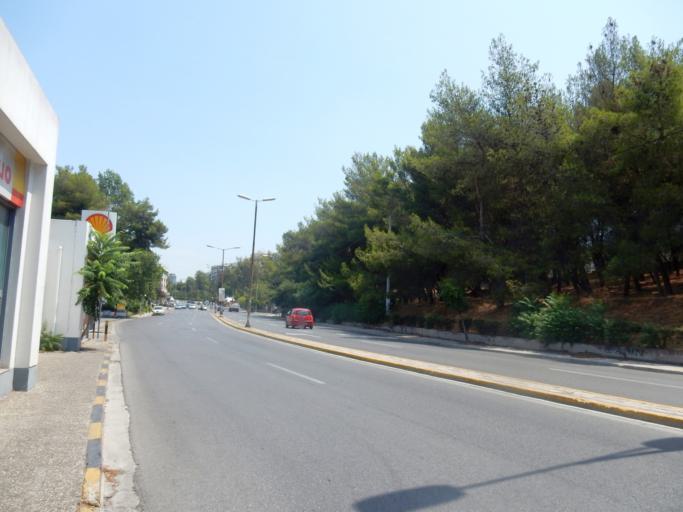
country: GR
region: Attica
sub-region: Nomarchia Athinas
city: Nea Ionia
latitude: 38.0361
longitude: 23.7484
